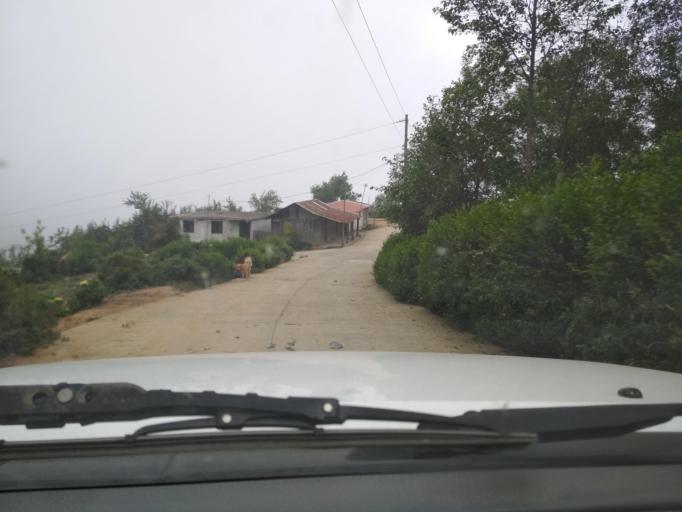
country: MX
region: Veracruz
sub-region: La Perla
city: Chilapa
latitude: 18.9946
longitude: -97.1449
